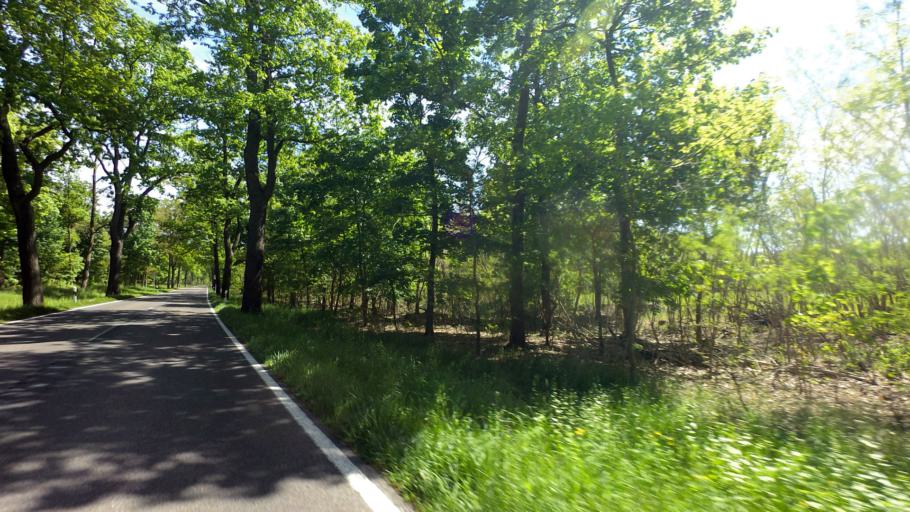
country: DE
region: Brandenburg
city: Sperenberg
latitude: 52.0483
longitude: 13.2956
